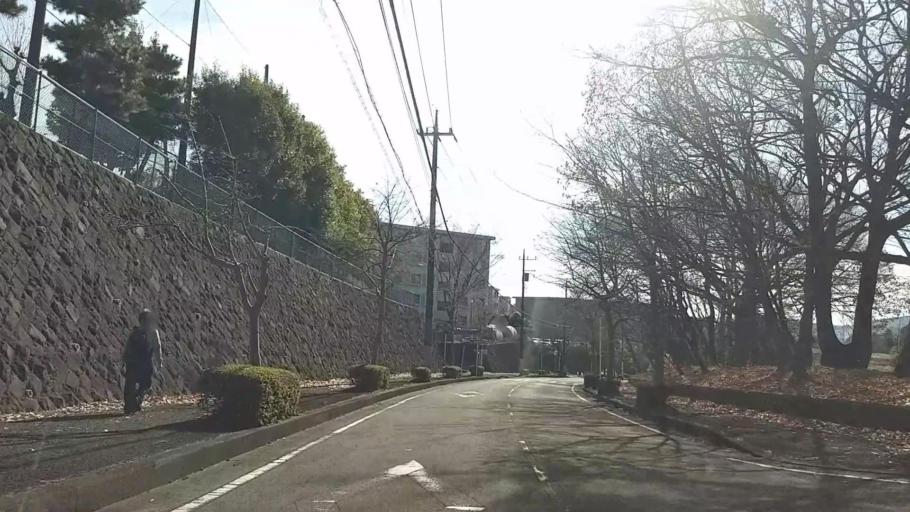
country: JP
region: Kanagawa
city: Hadano
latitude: 35.3564
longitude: 139.2239
